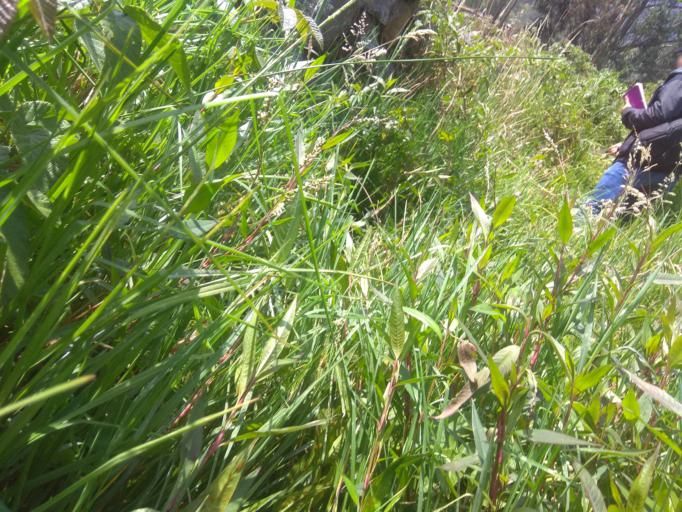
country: CO
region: Boyaca
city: Socha Viejo
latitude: 5.9812
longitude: -72.7208
